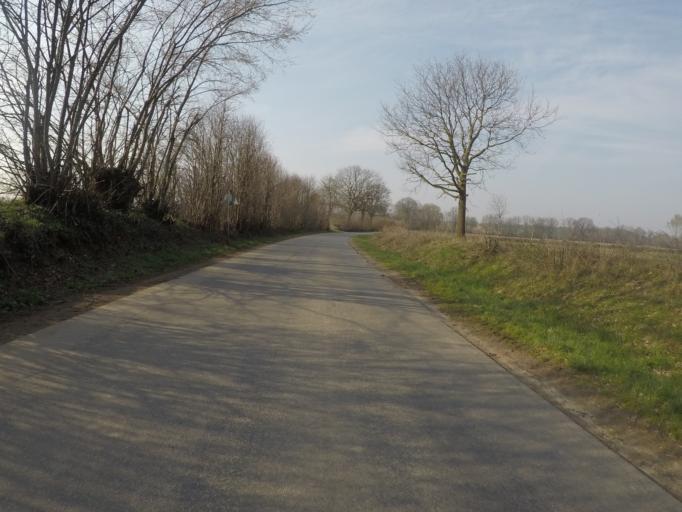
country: DE
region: Schleswig-Holstein
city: Leezen
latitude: 53.8749
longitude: 10.2393
